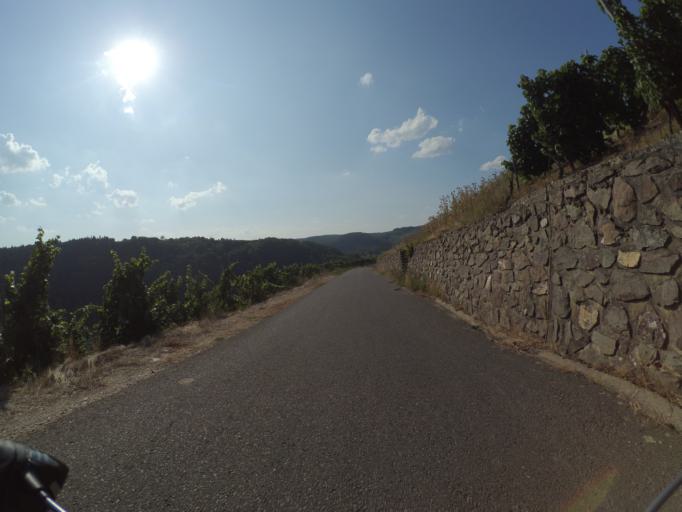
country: DE
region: Rheinland-Pfalz
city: Minheim
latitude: 49.8596
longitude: 6.9151
